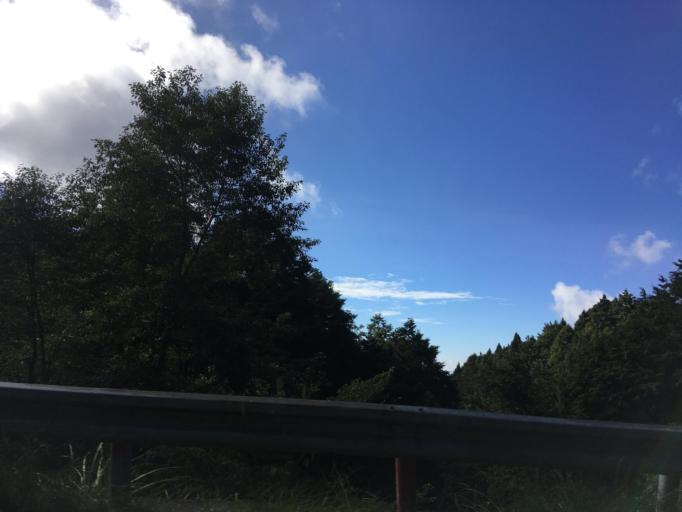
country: TW
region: Taiwan
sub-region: Yilan
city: Yilan
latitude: 24.5143
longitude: 121.5877
